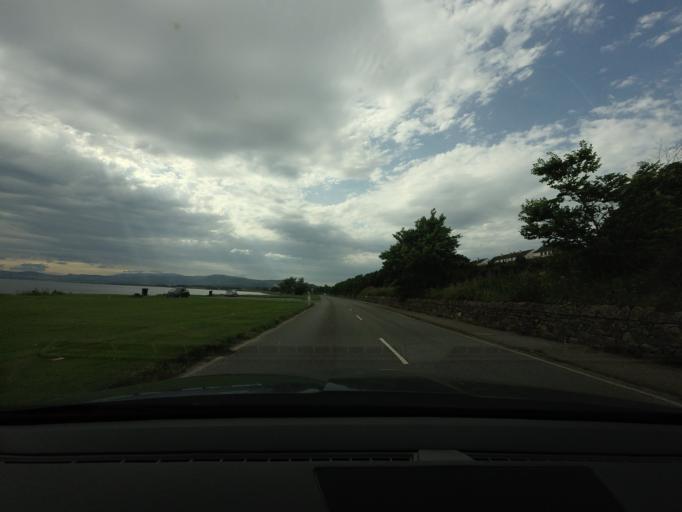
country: GB
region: Scotland
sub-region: Highland
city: Invergordon
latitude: 57.6898
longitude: -4.1822
